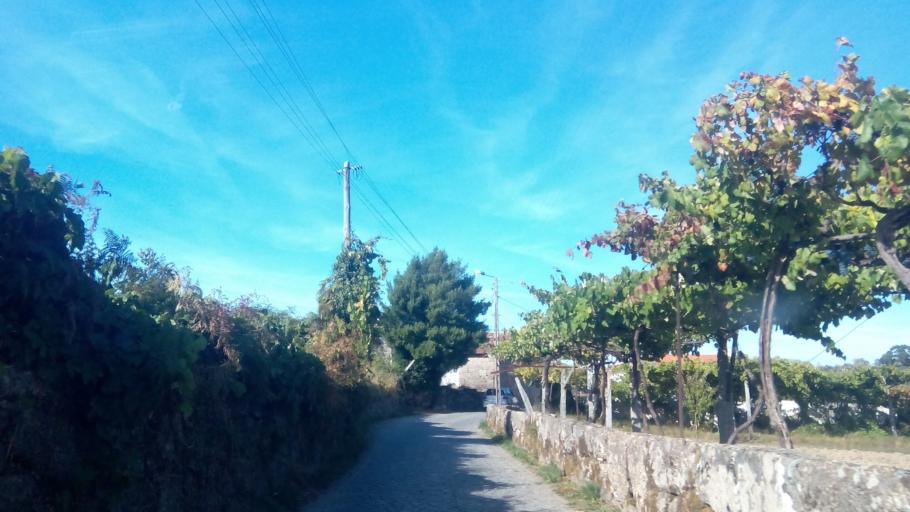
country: PT
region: Porto
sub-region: Paredes
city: Baltar
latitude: 41.1830
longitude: -8.3809
